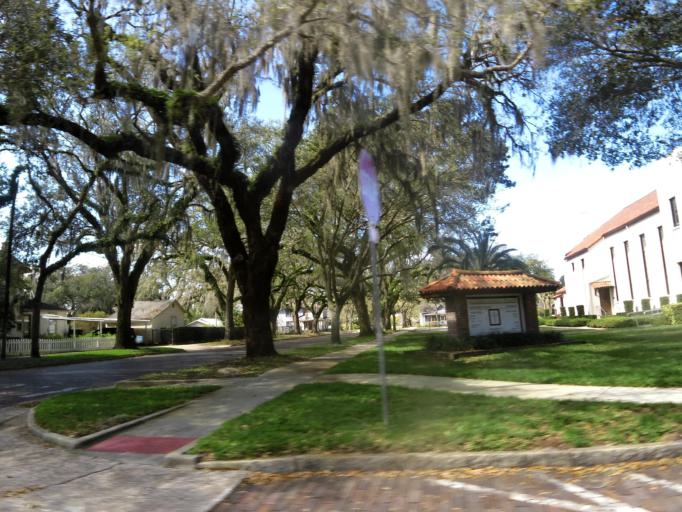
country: US
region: Florida
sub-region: Seminole County
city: Sanford
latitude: 28.8045
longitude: -81.2691
